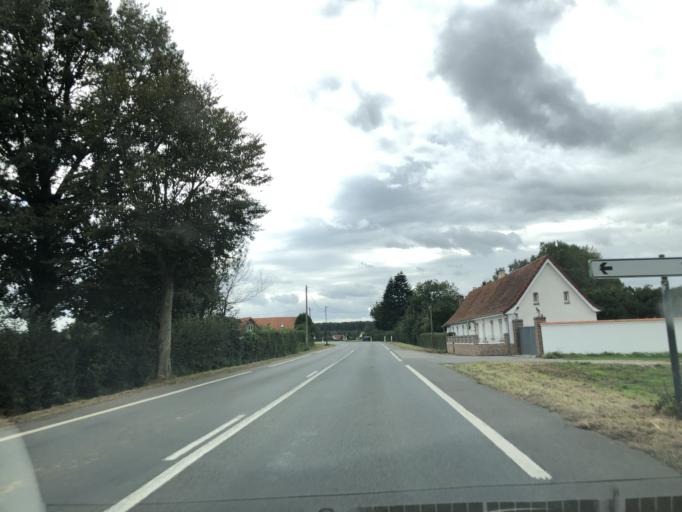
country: FR
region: Nord-Pas-de-Calais
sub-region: Departement du Pas-de-Calais
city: Hesdin
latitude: 50.4156
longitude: 2.0500
